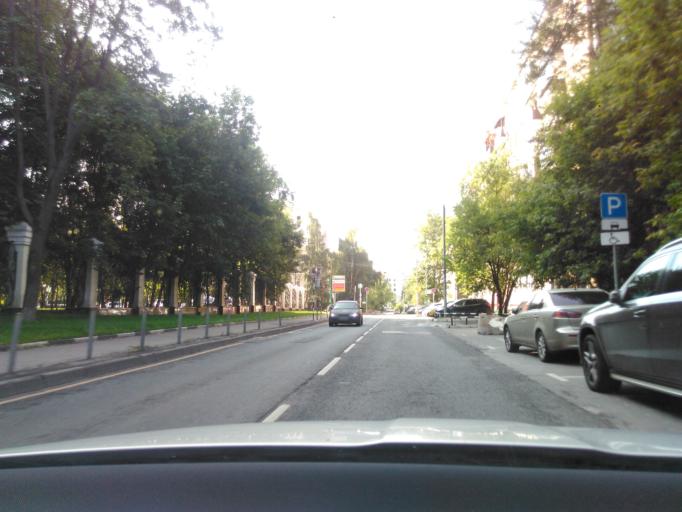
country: RU
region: Moscow
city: Sokol
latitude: 55.7977
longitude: 37.5190
